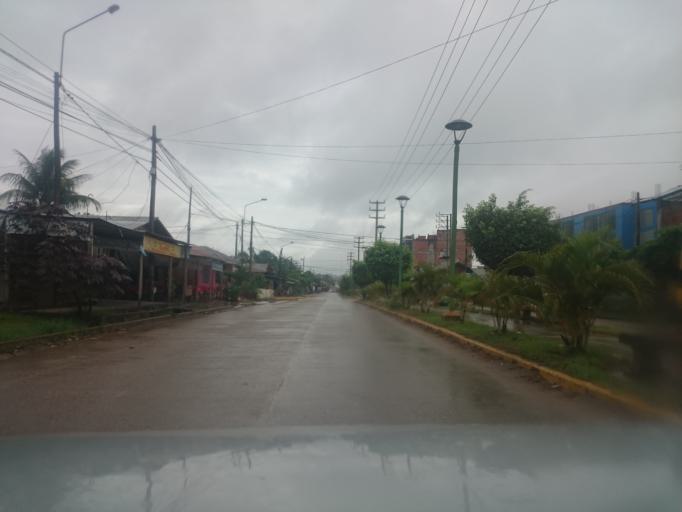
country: PE
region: Ucayali
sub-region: Provincia de Coronel Portillo
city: Pucallpa
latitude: -8.3824
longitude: -74.5509
